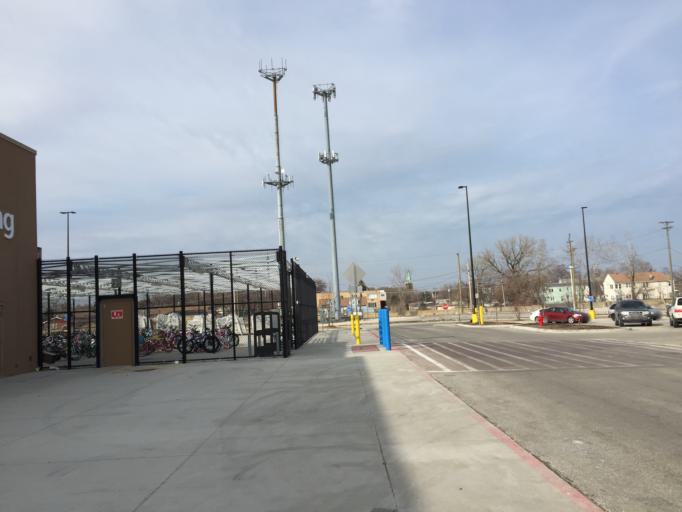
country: US
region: Illinois
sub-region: Cook County
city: Cicero
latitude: 41.8315
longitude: -87.7467
